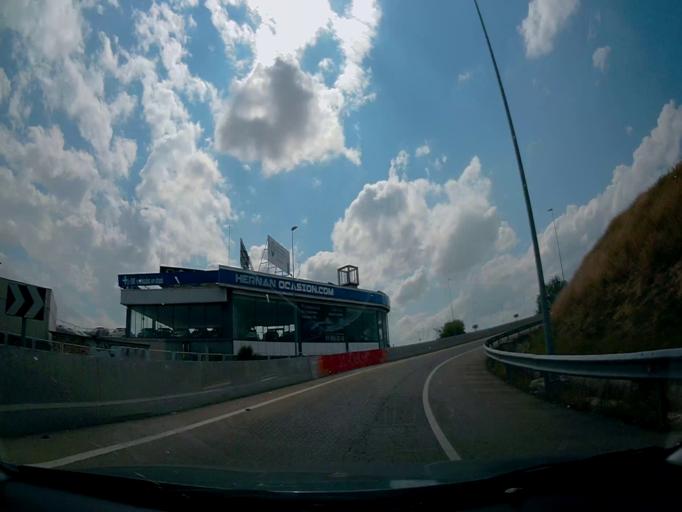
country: ES
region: Madrid
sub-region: Provincia de Madrid
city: Mostoles
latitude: 40.3440
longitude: -3.8597
